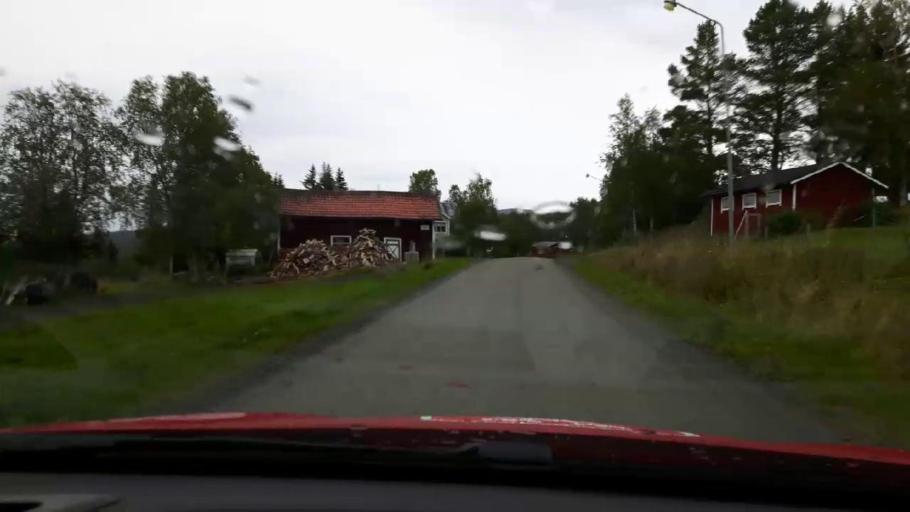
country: SE
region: Jaemtland
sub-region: Are Kommun
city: Are
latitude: 63.4703
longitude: 12.8098
